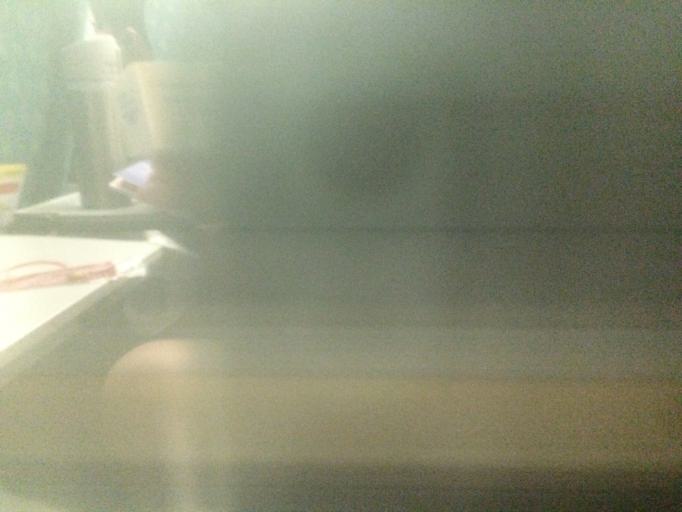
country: TW
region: Taiwan
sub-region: Miaoli
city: Miaoli
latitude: 24.4393
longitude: 120.6983
